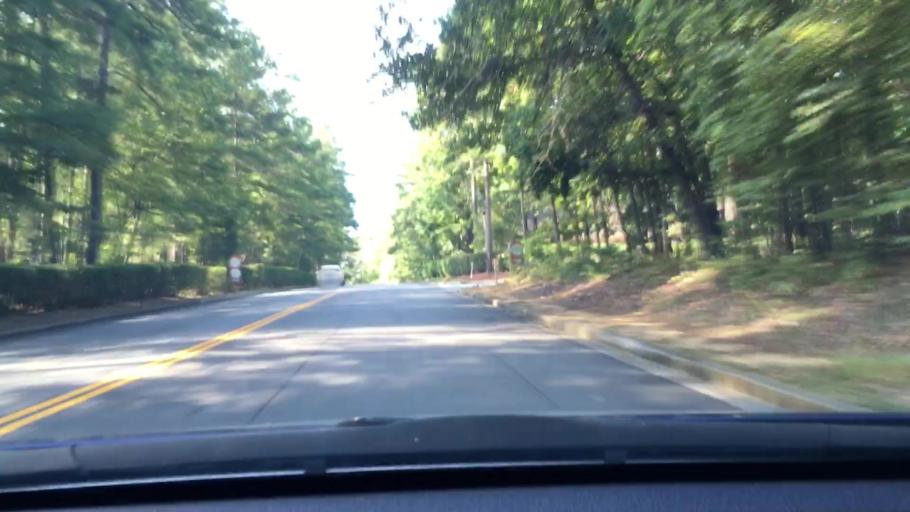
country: US
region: South Carolina
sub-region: Lexington County
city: Seven Oaks
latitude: 34.0809
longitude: -81.1394
